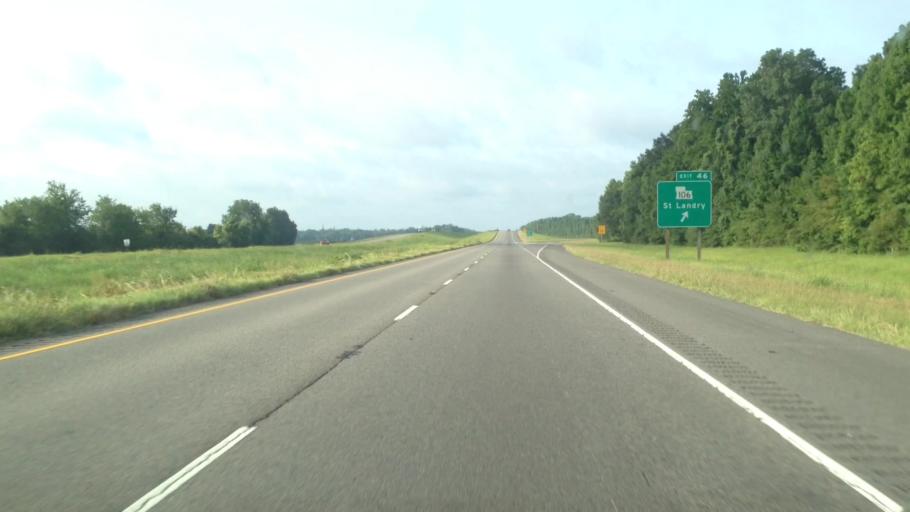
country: US
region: Louisiana
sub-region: Avoyelles Parish
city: Bunkie
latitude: 30.8724
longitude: -92.2280
